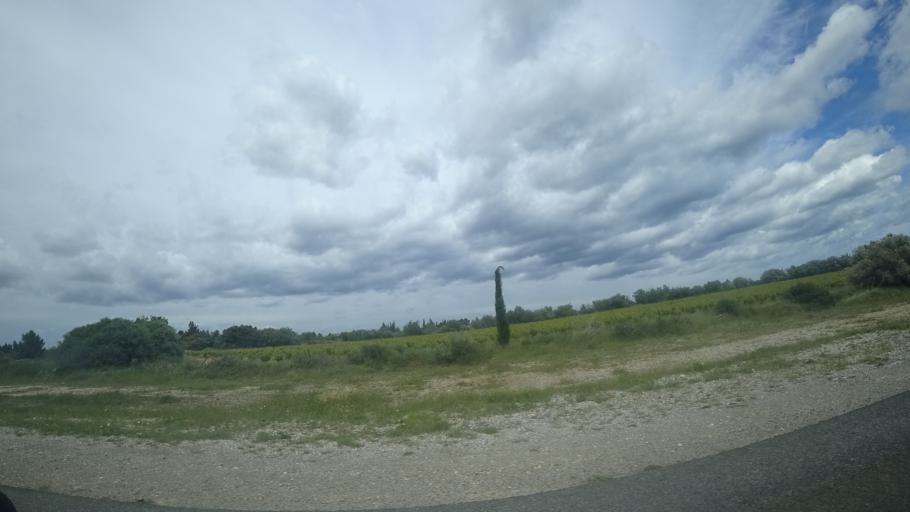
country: FR
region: Languedoc-Roussillon
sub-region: Departement de l'Aude
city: Leucate
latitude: 42.9186
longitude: 3.0199
